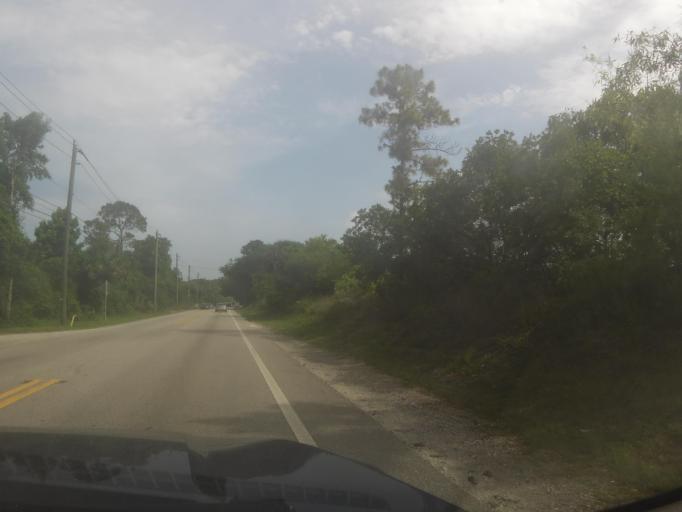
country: US
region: Florida
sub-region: Saint Johns County
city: Saint Augustine
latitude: 29.8815
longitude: -81.3517
